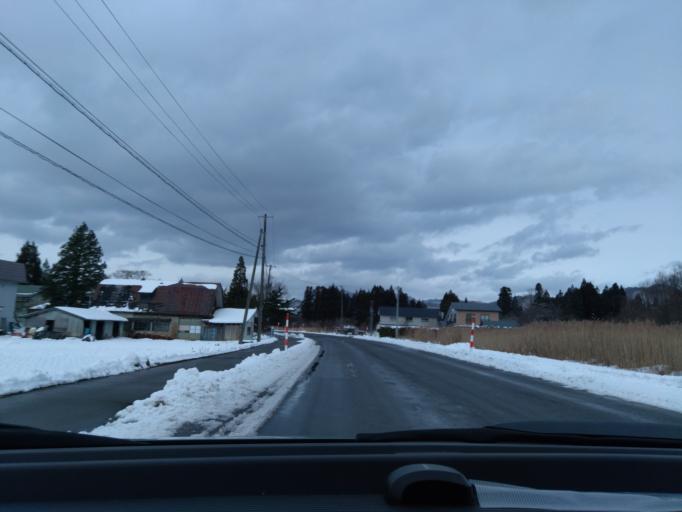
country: JP
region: Akita
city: Kakunodatemachi
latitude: 39.6193
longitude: 140.6314
